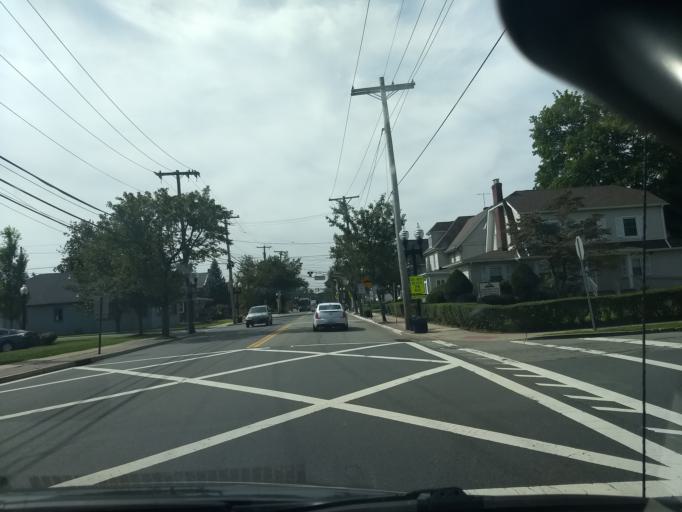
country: US
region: New Jersey
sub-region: Morris County
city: Morris Plains
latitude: 40.8271
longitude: -74.4797
